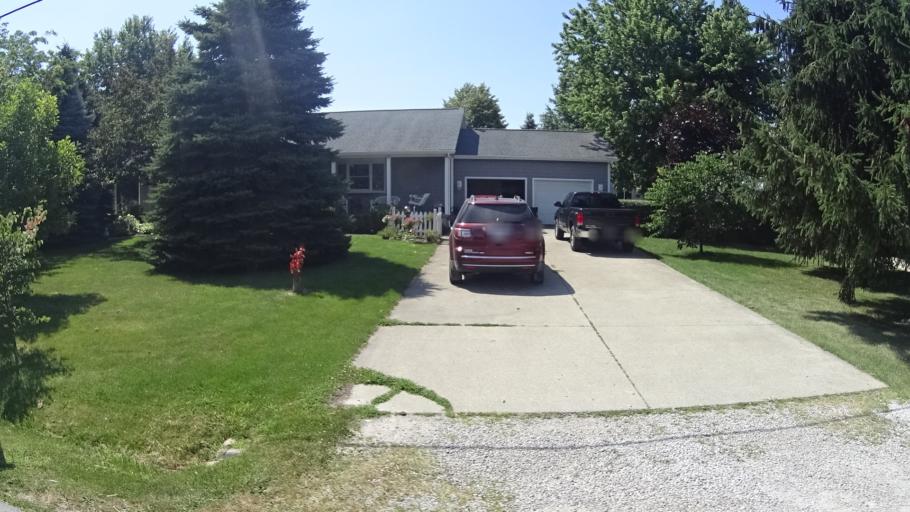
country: US
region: Ohio
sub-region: Erie County
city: Sandusky
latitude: 41.4317
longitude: -82.7797
